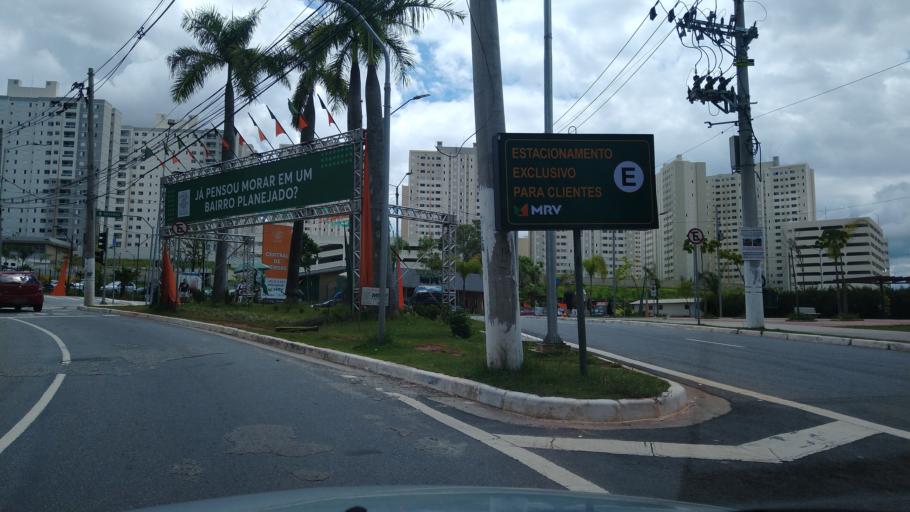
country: BR
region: Sao Paulo
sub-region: Osasco
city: Osasco
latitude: -23.5034
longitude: -46.7187
